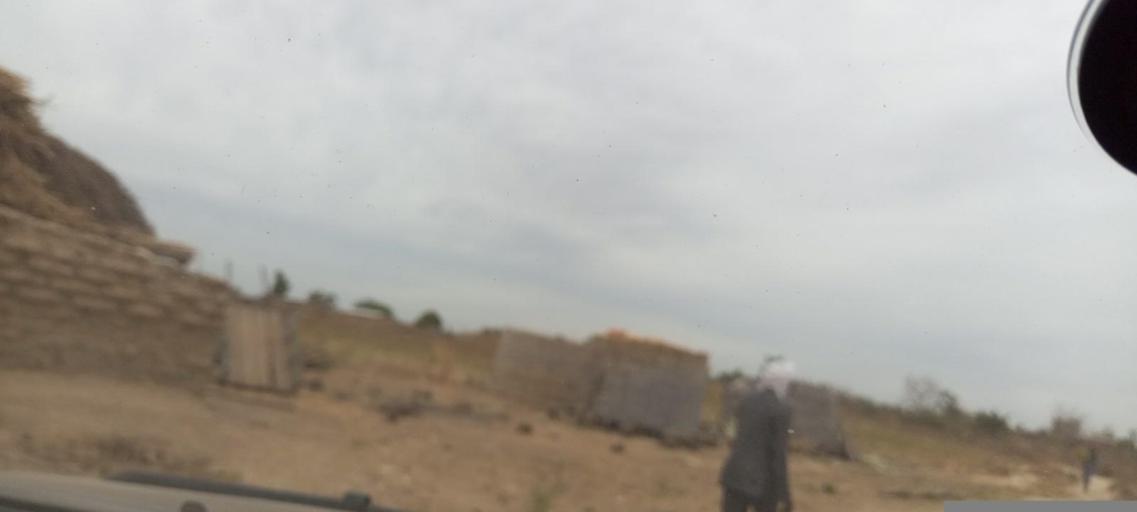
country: ML
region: Koulikoro
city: Kati
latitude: 12.7490
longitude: -8.3605
